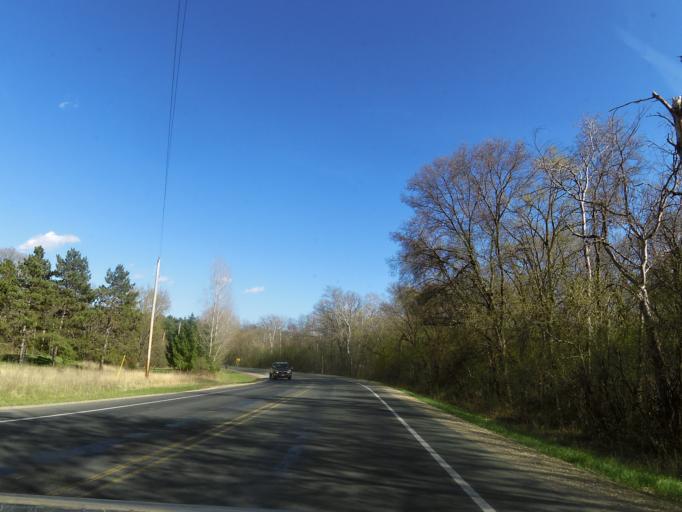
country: US
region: Wisconsin
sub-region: Saint Croix County
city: Somerset
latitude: 45.0266
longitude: -92.6593
